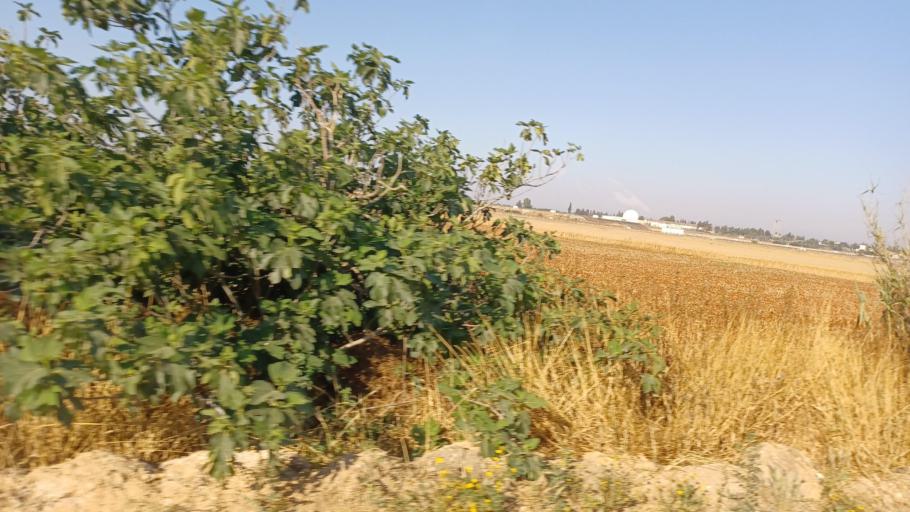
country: CY
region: Ammochostos
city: Famagusta
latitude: 35.0862
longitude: 33.9075
